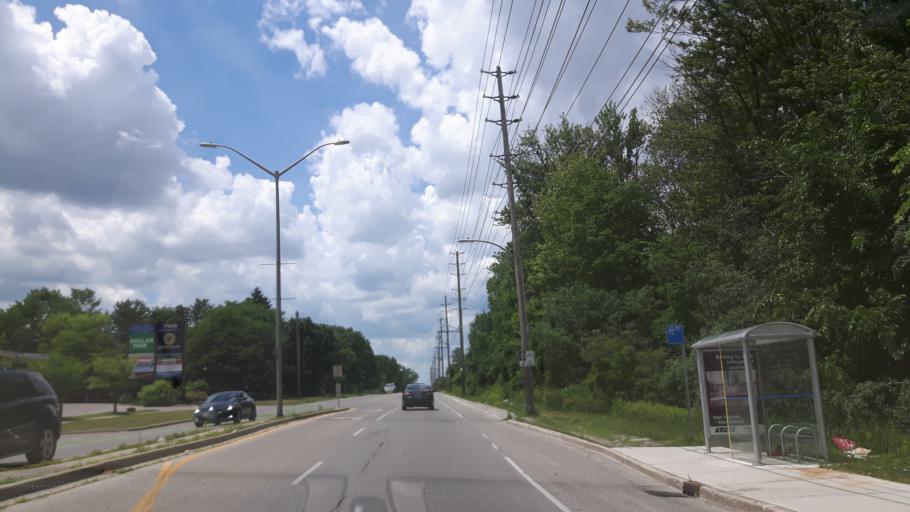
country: CA
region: Ontario
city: London
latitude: 42.9445
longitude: -81.2150
